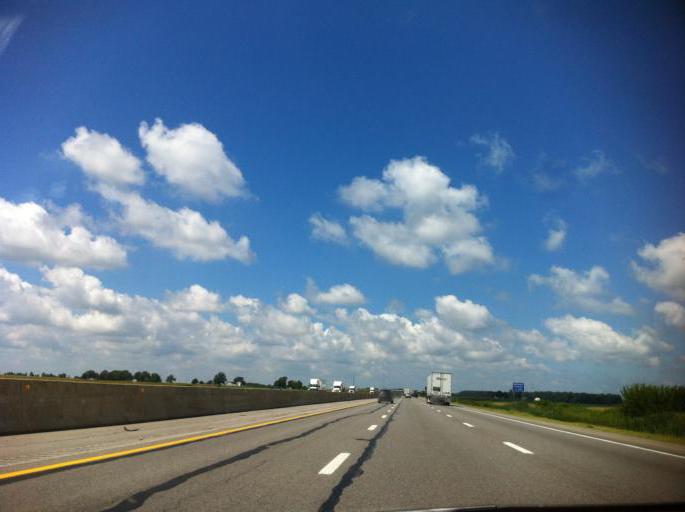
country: US
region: Ohio
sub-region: Erie County
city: Milan
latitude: 41.3309
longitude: -82.6591
